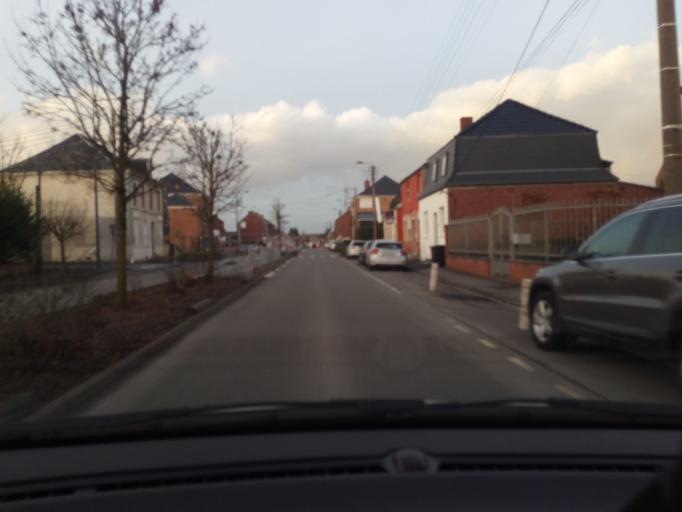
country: FR
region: Nord-Pas-de-Calais
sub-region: Departement du Nord
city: Maubeuge
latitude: 50.2858
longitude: 3.9748
